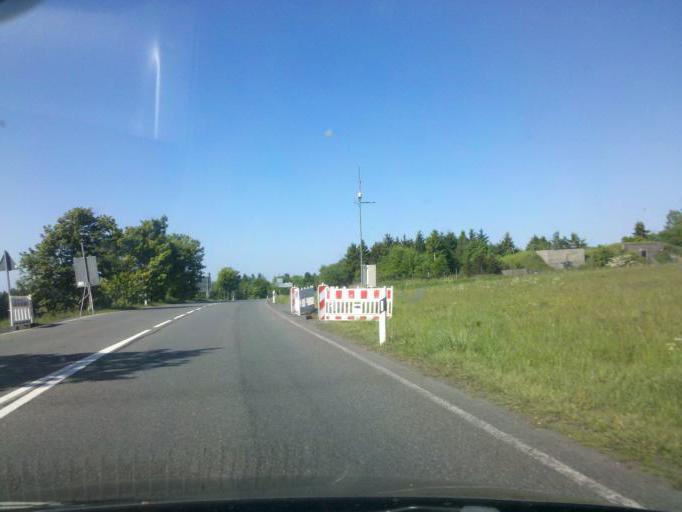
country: DE
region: Rheinland-Pfalz
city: Stein-Neukirch
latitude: 50.7052
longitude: 8.0677
